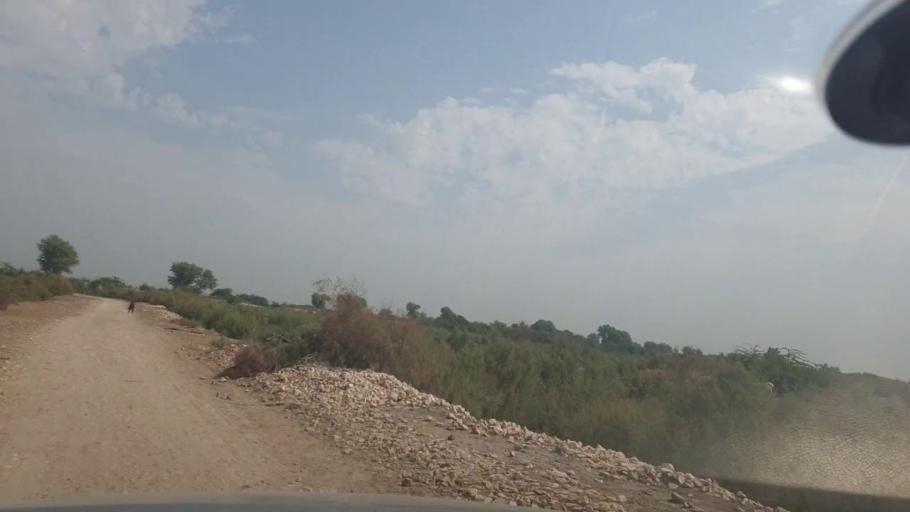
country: PK
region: Balochistan
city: Mehrabpur
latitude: 28.1158
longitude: 68.0911
